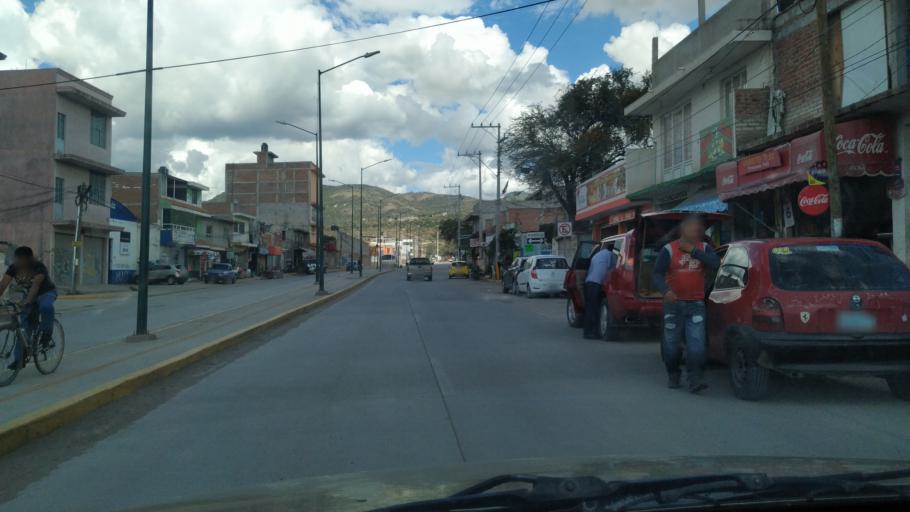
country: MX
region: Guanajuato
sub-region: Leon
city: Medina
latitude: 21.1500
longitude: -101.6291
